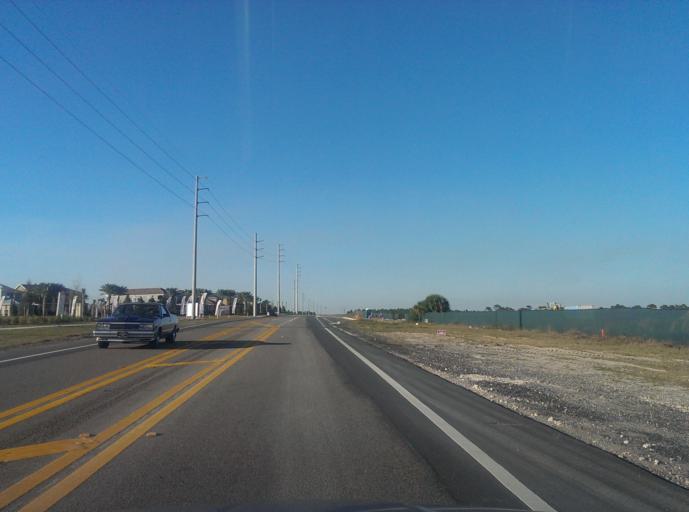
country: US
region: Florida
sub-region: Polk County
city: Loughman
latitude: 28.2884
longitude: -81.5905
